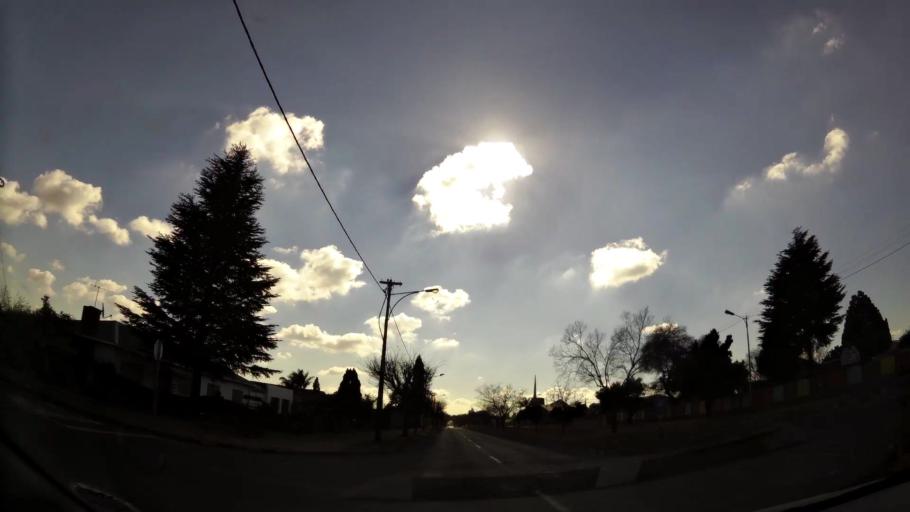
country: ZA
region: Gauteng
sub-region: City of Johannesburg Metropolitan Municipality
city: Roodepoort
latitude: -26.1357
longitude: 27.8301
